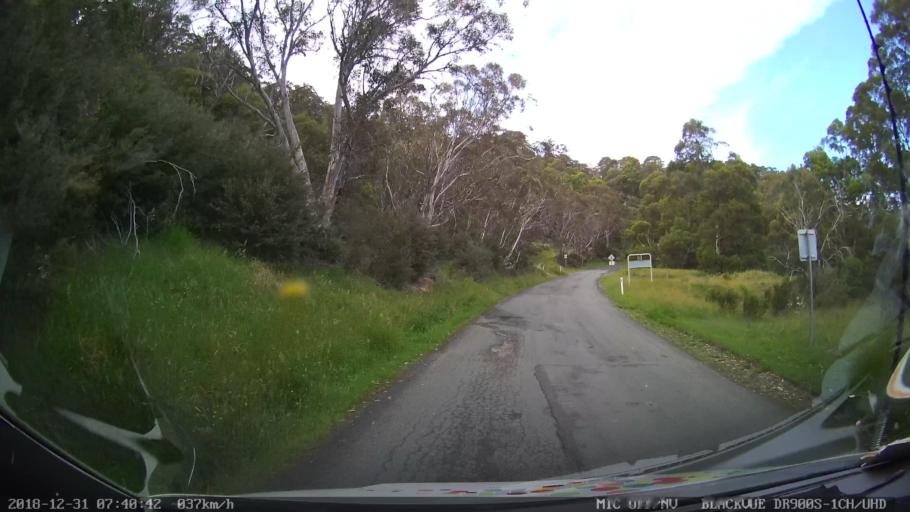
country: AU
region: New South Wales
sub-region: Snowy River
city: Jindabyne
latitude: -36.3519
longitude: 148.4159
